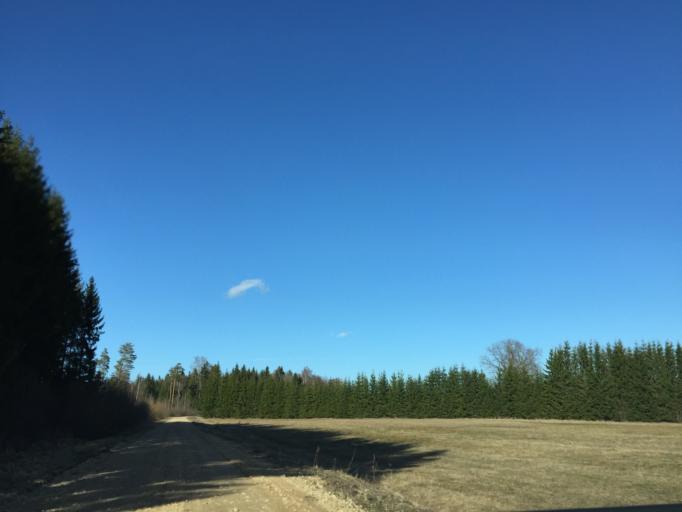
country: LV
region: Ogre
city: Ogre
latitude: 56.8834
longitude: 24.7112
